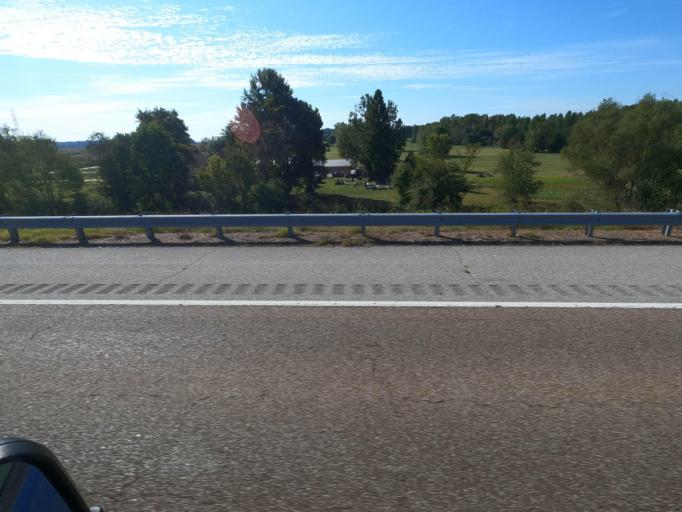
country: US
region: Tennessee
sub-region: Shelby County
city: Millington
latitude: 35.3086
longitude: -89.8364
